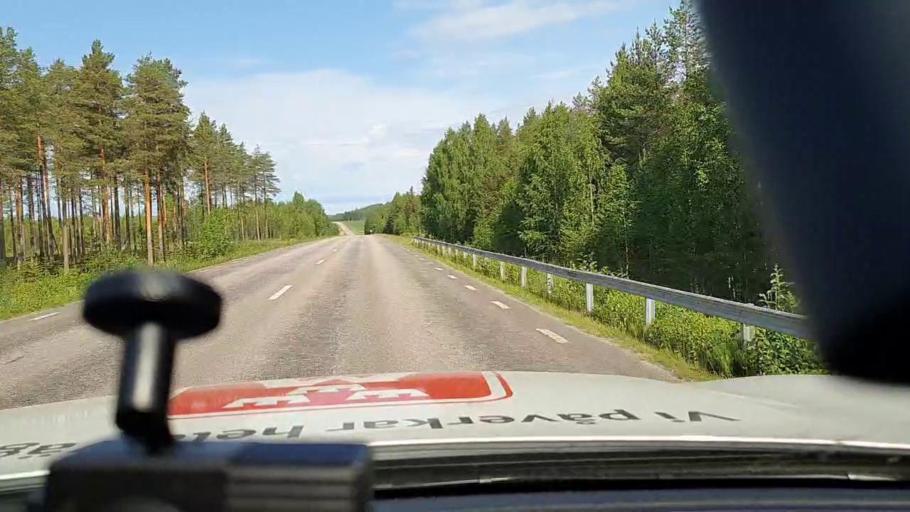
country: SE
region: Norrbotten
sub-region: Bodens Kommun
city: Boden
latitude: 65.9073
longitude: 21.3584
